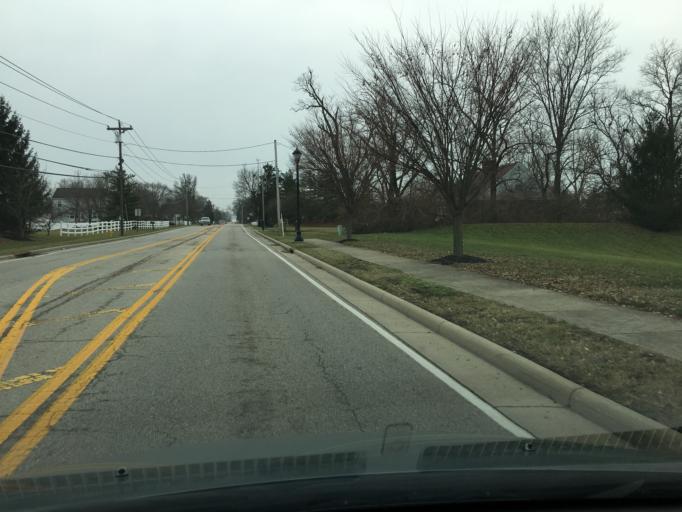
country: US
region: Ohio
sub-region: Warren County
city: Mason
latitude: 39.3269
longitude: -84.3308
